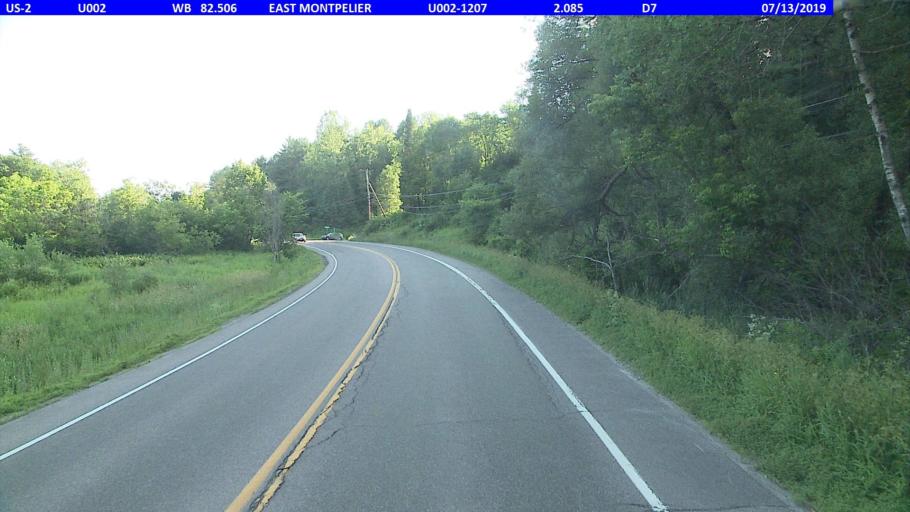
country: US
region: Vermont
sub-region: Washington County
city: Barre
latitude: 44.2637
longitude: -72.5000
